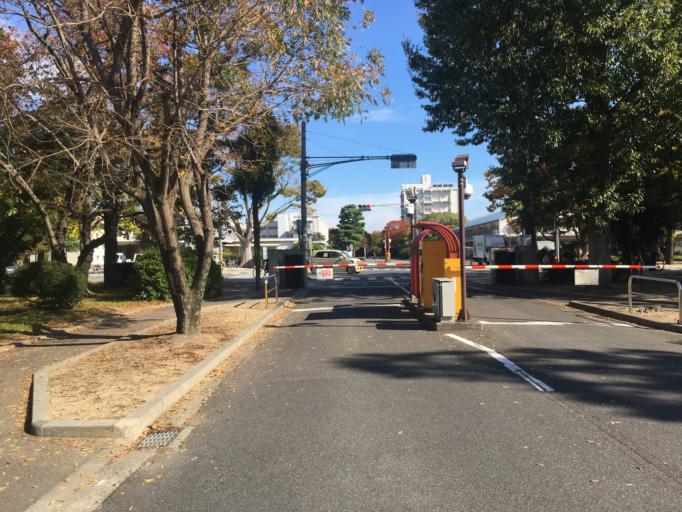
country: JP
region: Okayama
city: Okayama-shi
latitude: 34.6864
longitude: 133.9193
